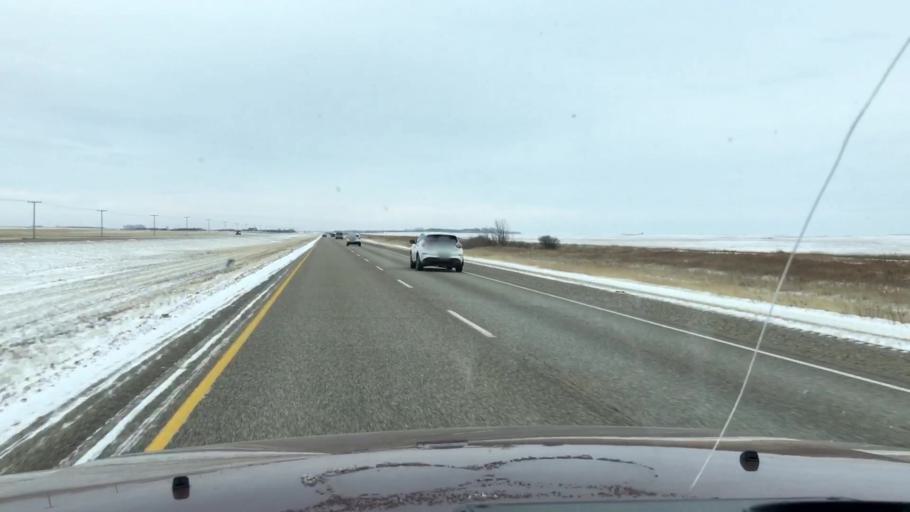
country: CA
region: Saskatchewan
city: Moose Jaw
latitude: 50.9949
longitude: -105.7578
